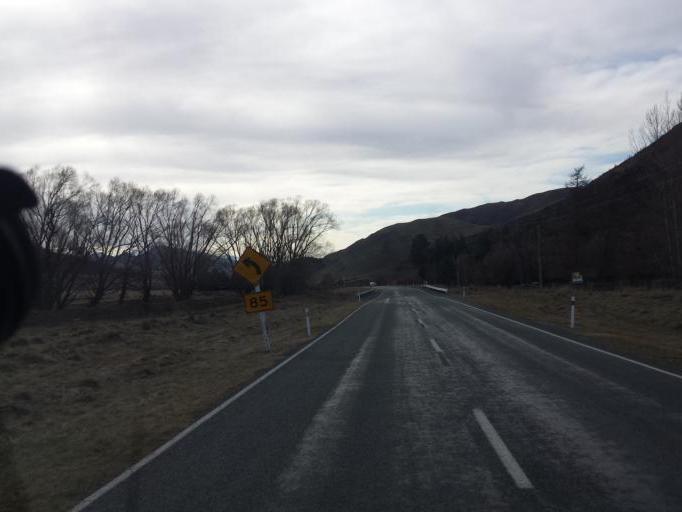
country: NZ
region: Canterbury
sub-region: Timaru District
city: Pleasant Point
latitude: -44.0816
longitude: 170.6618
